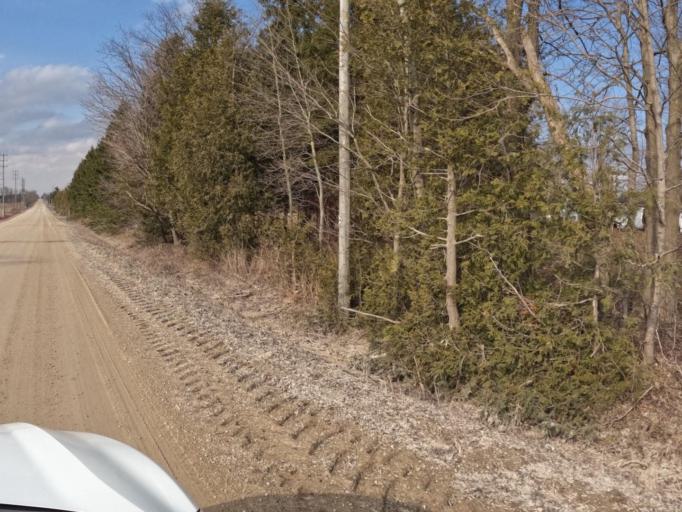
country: CA
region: Ontario
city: Shelburne
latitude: 43.9054
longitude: -80.3024
